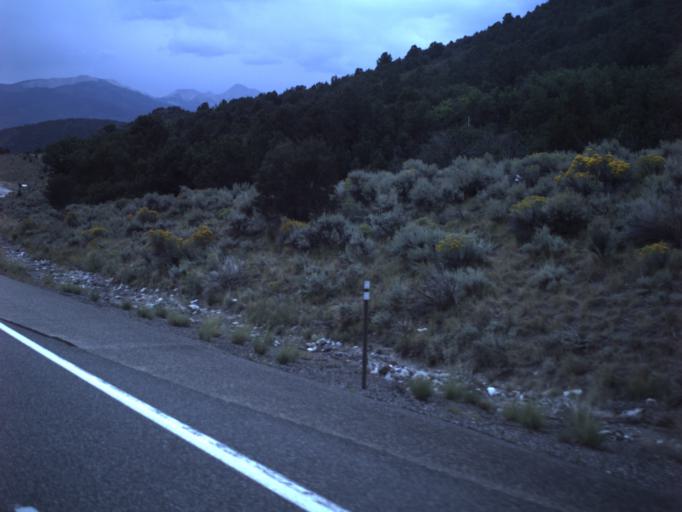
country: US
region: Utah
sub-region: Beaver County
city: Beaver
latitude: 38.5902
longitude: -112.4932
